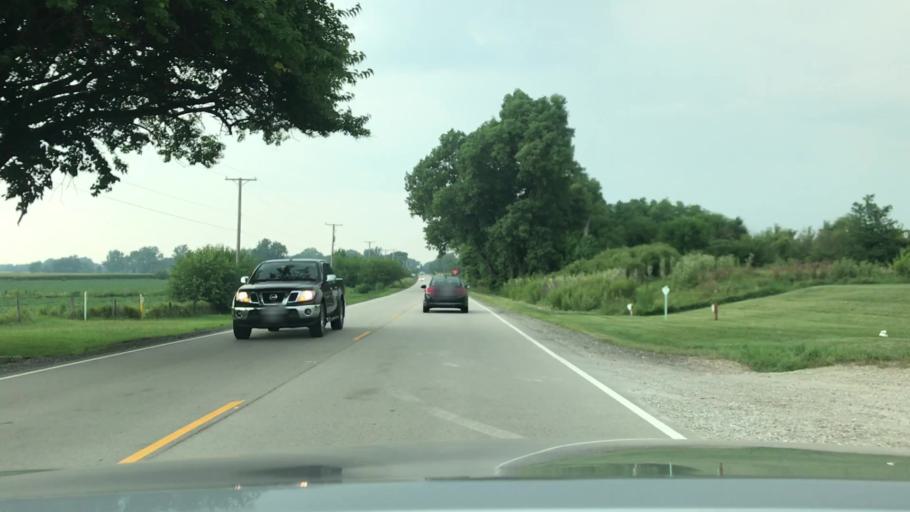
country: US
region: Illinois
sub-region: Will County
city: Plainfield
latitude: 41.6583
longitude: -88.2353
